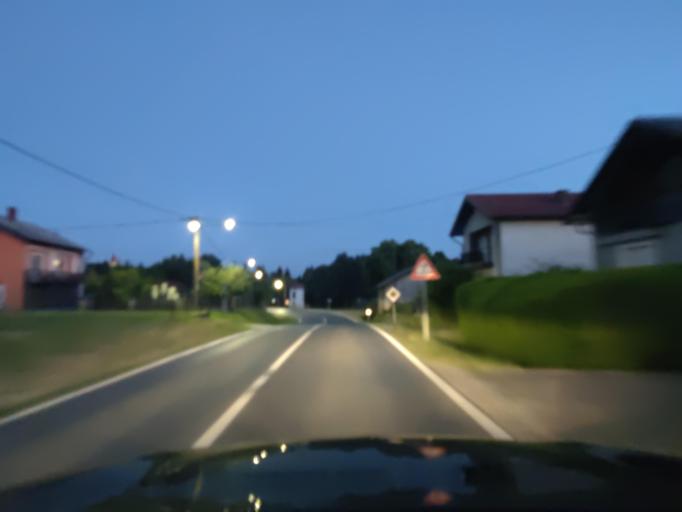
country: HR
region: Medimurska
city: Vratisinec
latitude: 46.4738
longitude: 16.4231
